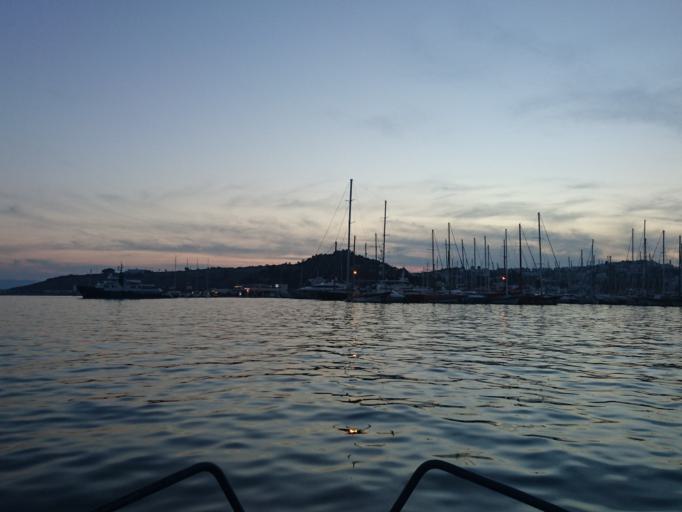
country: TR
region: Mugla
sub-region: Bodrum
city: Bodrum
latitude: 37.0346
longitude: 27.4275
